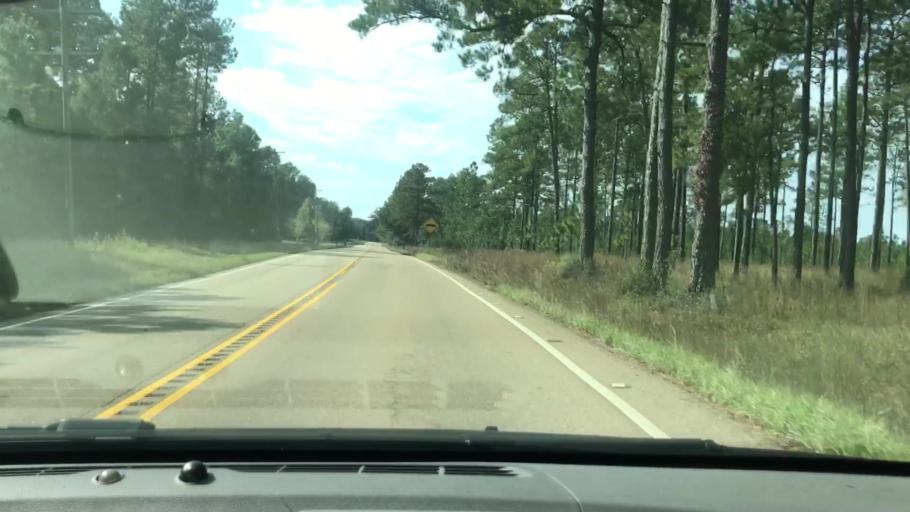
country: US
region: Louisiana
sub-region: Saint Tammany Parish
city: Abita Springs
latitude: 30.5150
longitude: -89.9444
